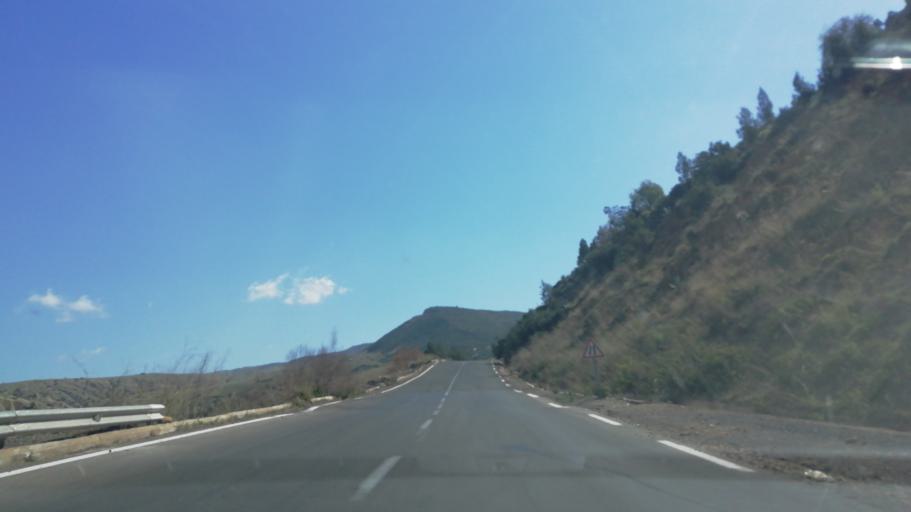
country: DZ
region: Mascara
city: Mascara
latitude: 35.4998
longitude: 0.1323
